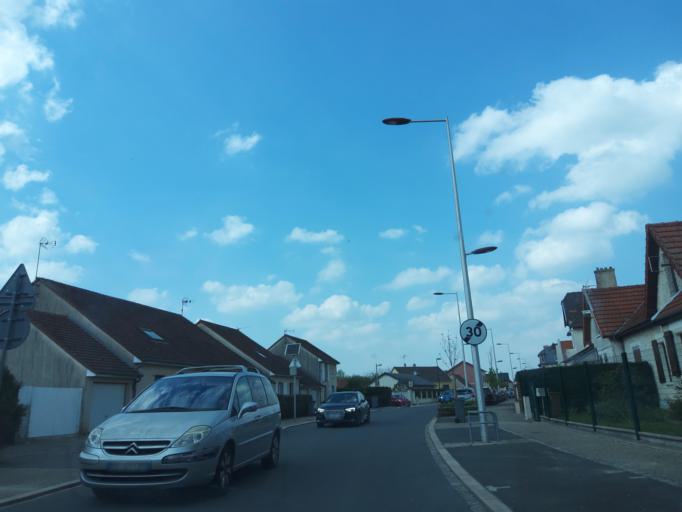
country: FR
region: Picardie
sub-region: Departement de l'Aisne
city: Laon
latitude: 49.5780
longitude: 3.6308
